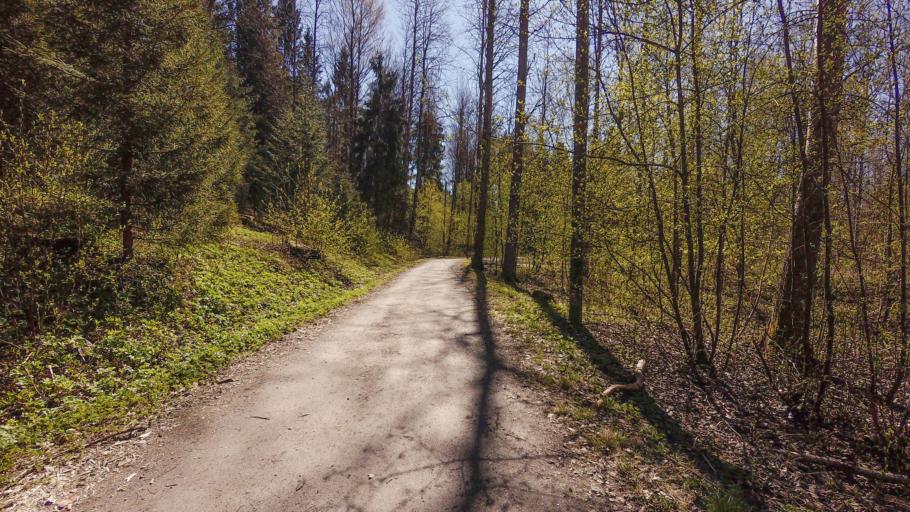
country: FI
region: Uusimaa
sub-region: Helsinki
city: Vantaa
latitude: 60.2252
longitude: 25.1333
